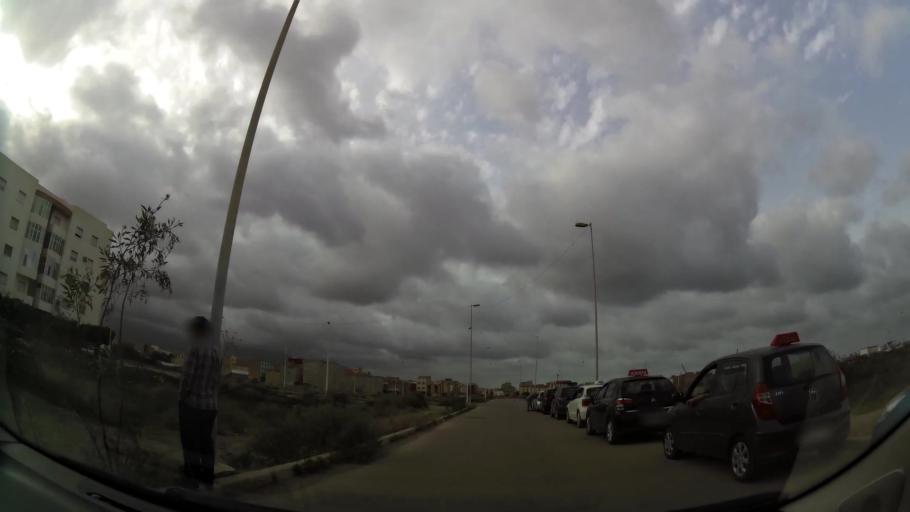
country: MA
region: Oriental
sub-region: Nador
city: Nador
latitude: 35.1549
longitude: -2.9106
